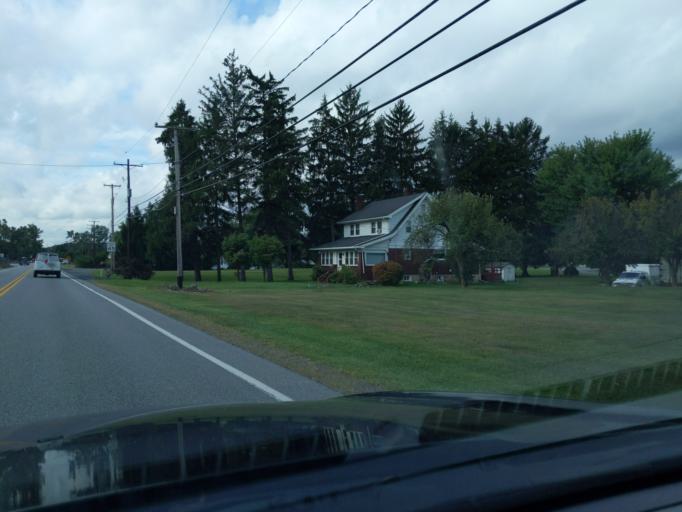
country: US
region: Pennsylvania
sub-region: Blair County
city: Roaring Spring
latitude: 40.3712
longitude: -78.4251
